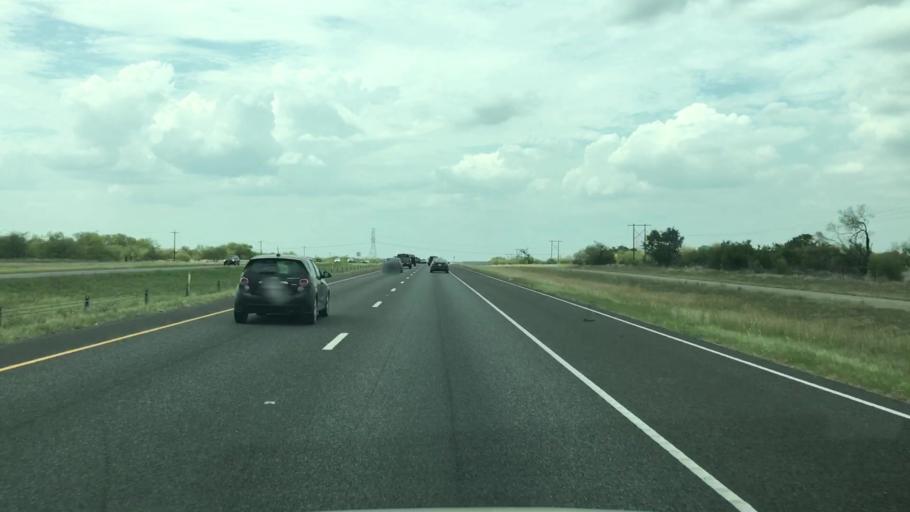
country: US
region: Texas
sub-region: Atascosa County
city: Pleasanton
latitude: 28.8149
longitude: -98.3558
